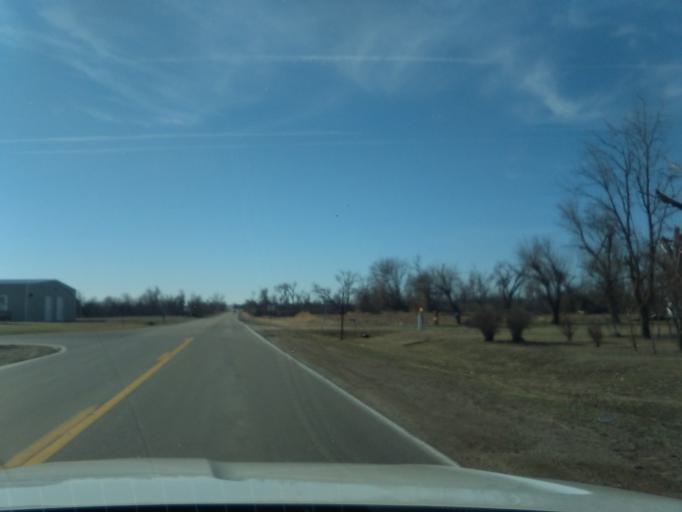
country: US
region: Nebraska
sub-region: Saline County
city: Friend
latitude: 40.7789
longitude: -97.2923
